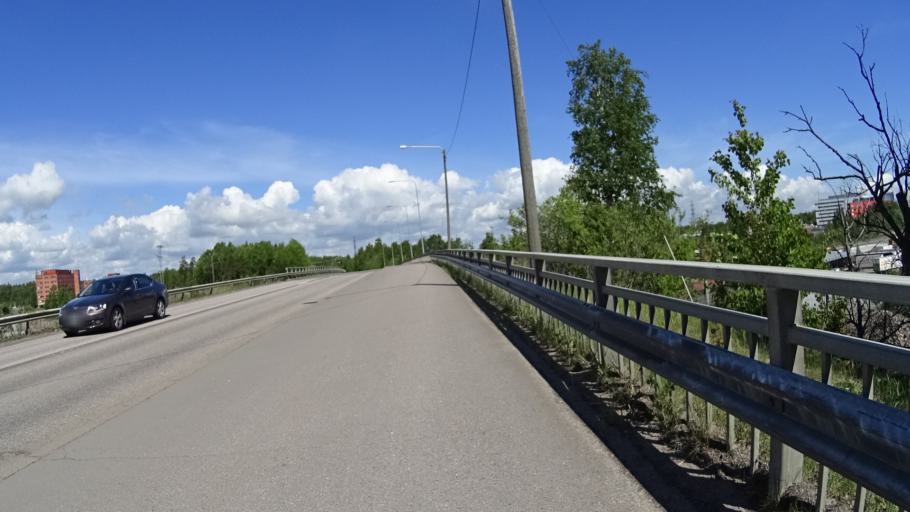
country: FI
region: Uusimaa
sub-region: Helsinki
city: Helsinki
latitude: 60.2164
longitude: 24.9340
